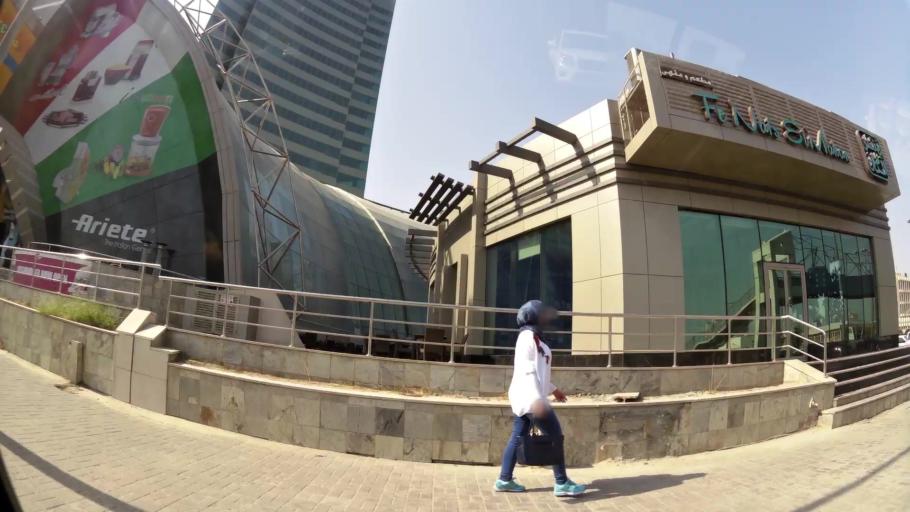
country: KW
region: Muhafazat Hawalli
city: Hawalli
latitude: 29.3408
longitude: 48.0289
